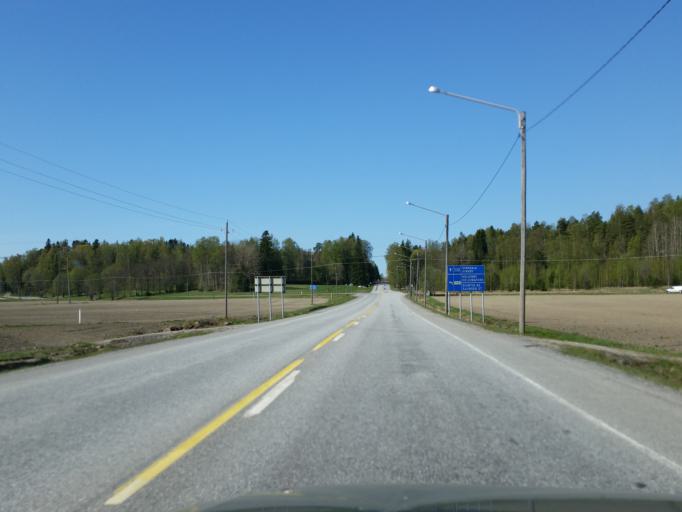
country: FI
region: Uusimaa
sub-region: Helsinki
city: Siuntio
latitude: 60.1722
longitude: 24.2046
